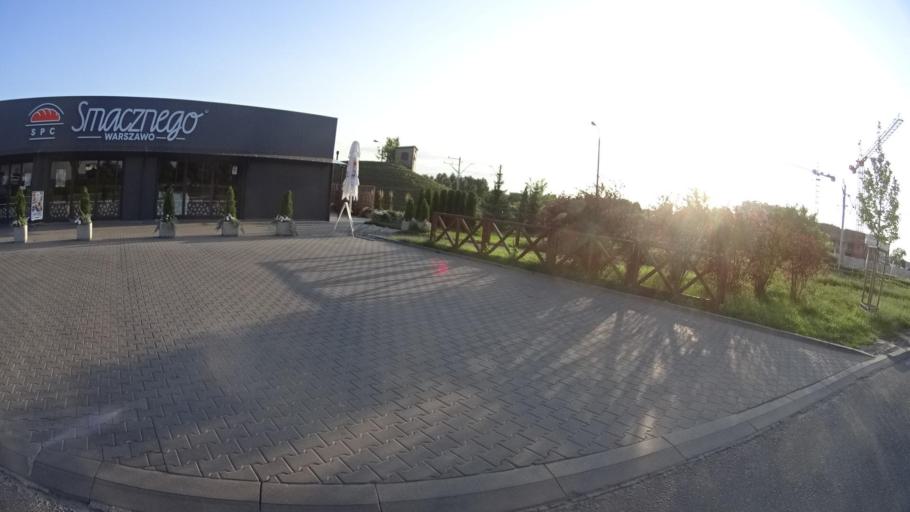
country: PL
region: Masovian Voivodeship
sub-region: Warszawa
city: Wlochy
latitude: 52.1921
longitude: 20.9337
